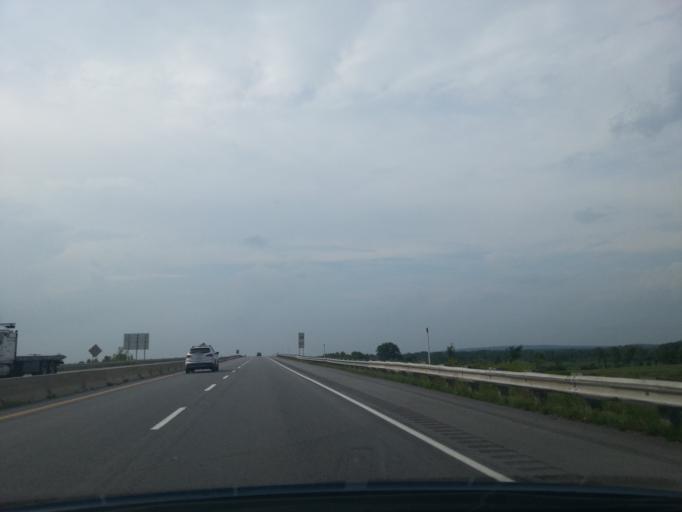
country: CA
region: Quebec
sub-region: Monteregie
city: Rigaud
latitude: 45.4795
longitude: -74.2848
